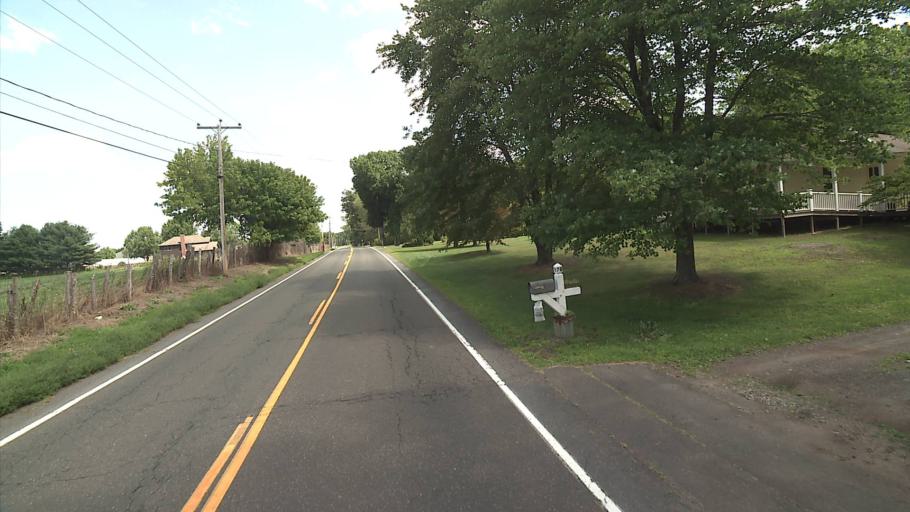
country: US
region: Connecticut
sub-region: Hartford County
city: Windsor Locks
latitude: 41.8963
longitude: -72.5930
